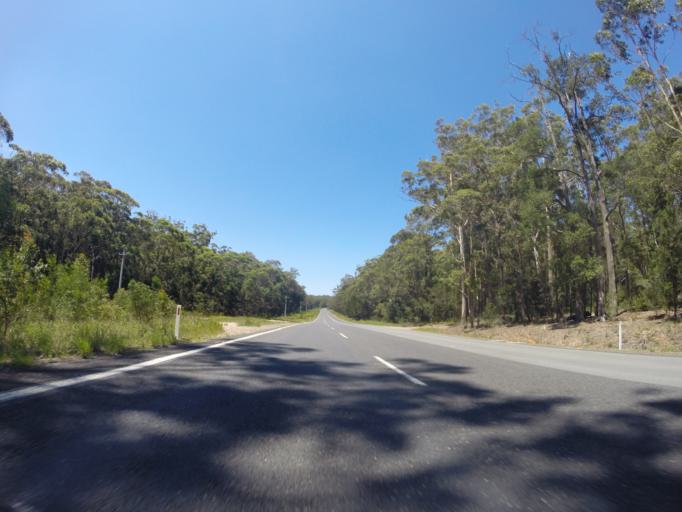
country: AU
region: New South Wales
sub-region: Shoalhaven Shire
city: Ulladulla
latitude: -35.4533
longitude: 150.3765
